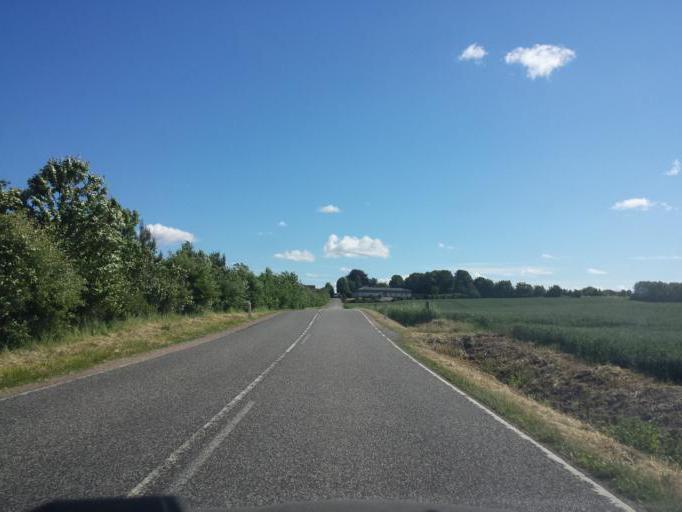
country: DK
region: Capital Region
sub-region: Egedal Kommune
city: Ganlose
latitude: 55.8026
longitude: 12.2644
